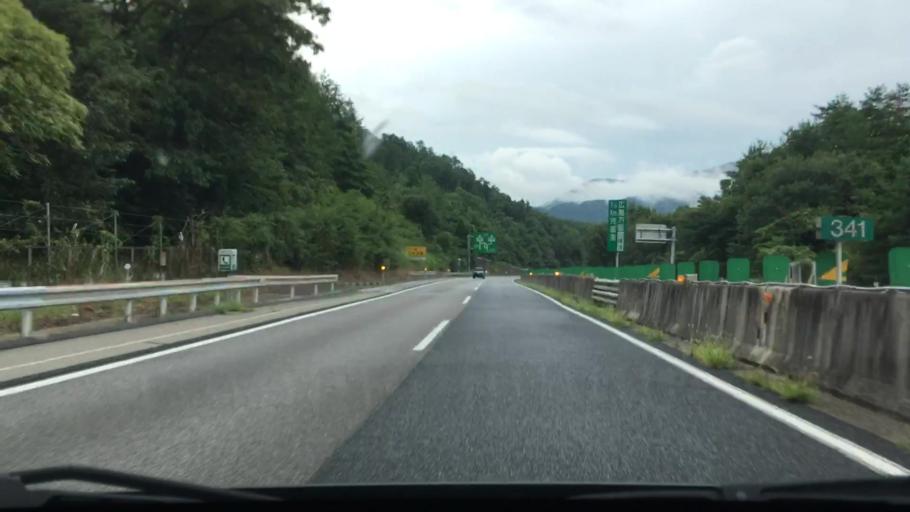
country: JP
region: Hiroshima
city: Hiroshima-shi
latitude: 34.5845
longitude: 132.4745
